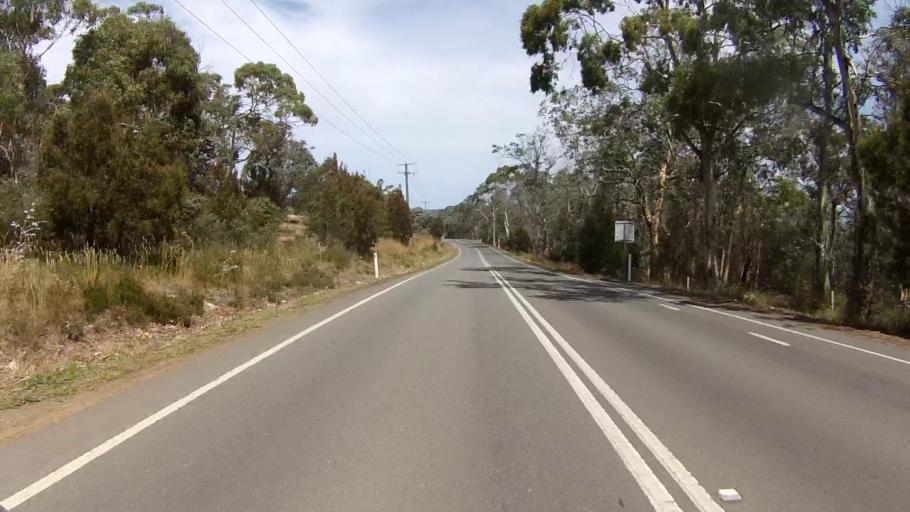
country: AU
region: Tasmania
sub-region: Clarence
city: Sandford
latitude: -42.9772
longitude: 147.5027
